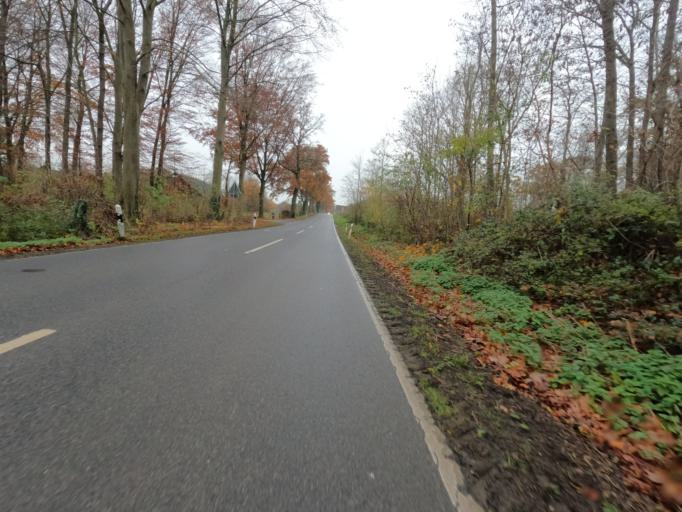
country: DE
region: North Rhine-Westphalia
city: Geilenkirchen
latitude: 50.9868
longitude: 6.1512
